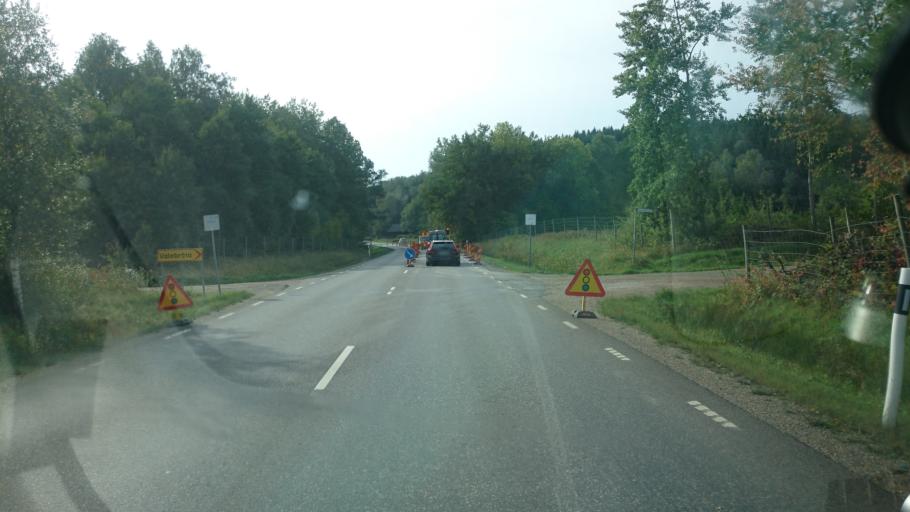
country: SE
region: Vaestra Goetaland
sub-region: Alingsas Kommun
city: Alingsas
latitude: 57.9866
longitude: 12.4393
